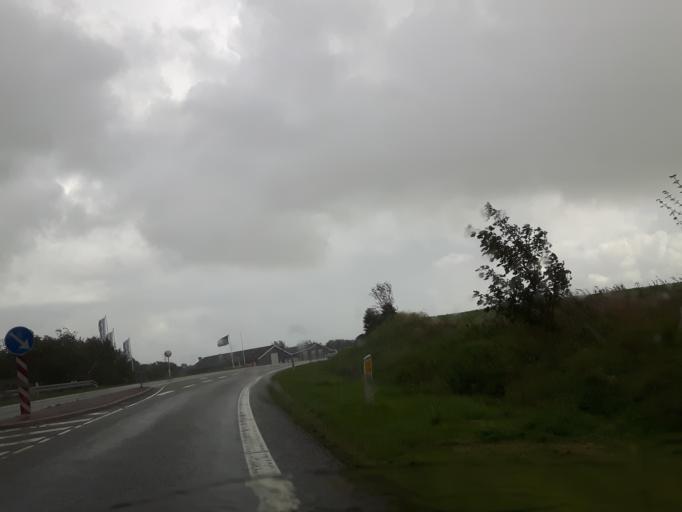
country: DK
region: North Denmark
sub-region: Thisted Kommune
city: Hurup
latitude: 56.6376
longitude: 8.5094
